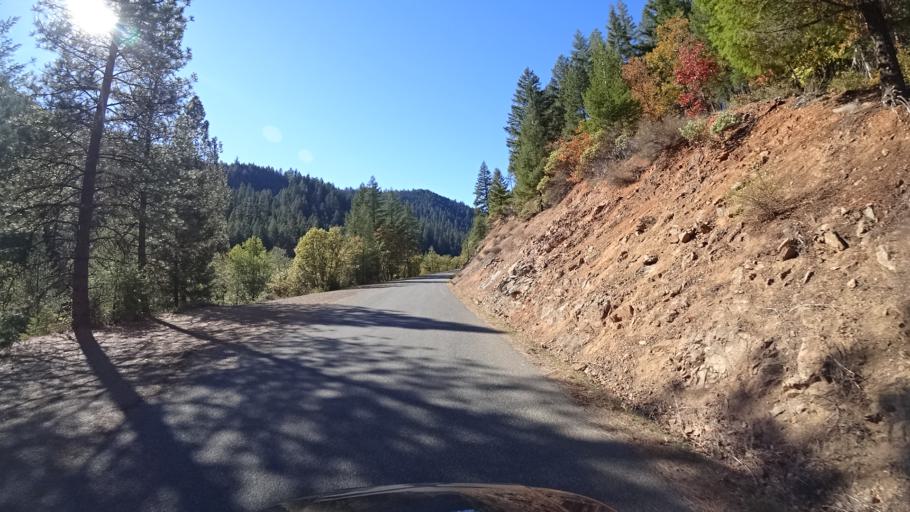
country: US
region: California
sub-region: Siskiyou County
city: Happy Camp
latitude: 41.3027
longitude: -123.1589
